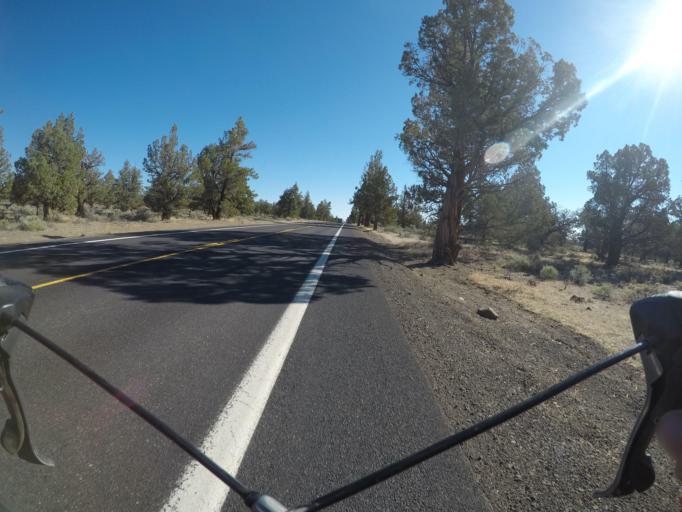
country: US
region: Oregon
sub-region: Deschutes County
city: Redmond
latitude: 44.2155
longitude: -121.3151
